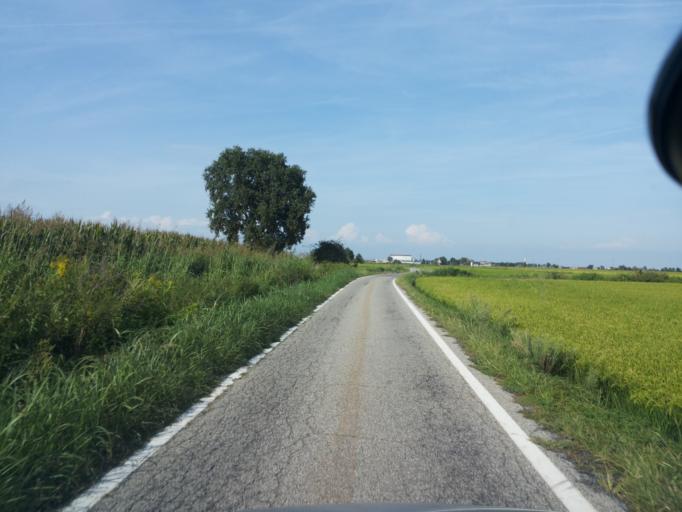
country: IT
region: Piedmont
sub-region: Provincia di Vercelli
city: San Germano Vercellese
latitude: 45.3359
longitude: 8.2332
